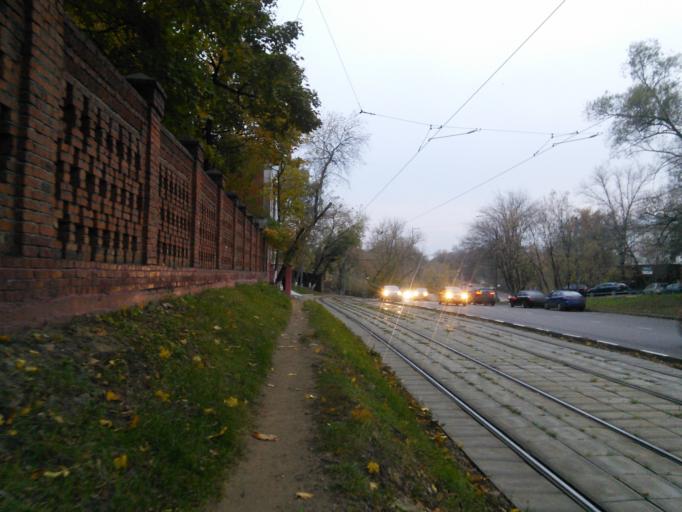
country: RU
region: Moscow
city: Lefortovo
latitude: 55.7712
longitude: 37.7055
